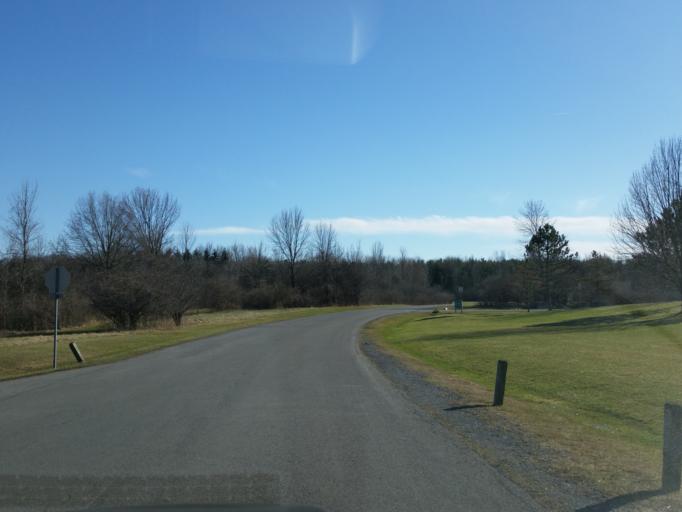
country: US
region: New York
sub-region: Monroe County
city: Scottsville
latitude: 43.0836
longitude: -77.7976
